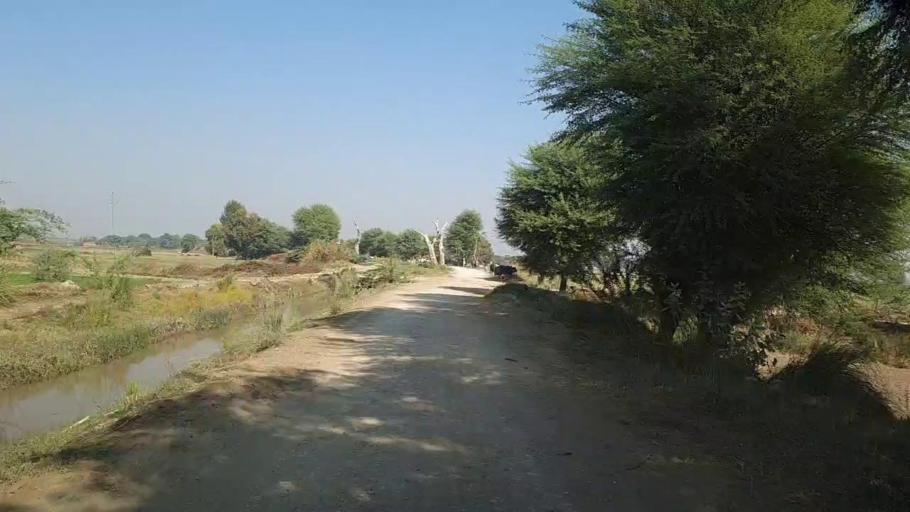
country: PK
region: Sindh
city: Bozdar
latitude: 27.1958
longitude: 68.6374
